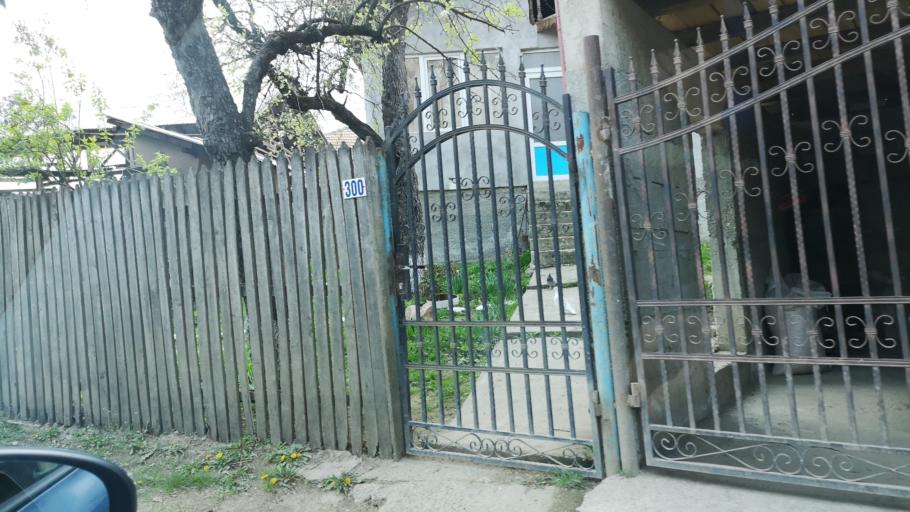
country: RO
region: Prahova
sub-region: Comuna Soimari
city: Soimari
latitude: 45.1789
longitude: 26.2168
